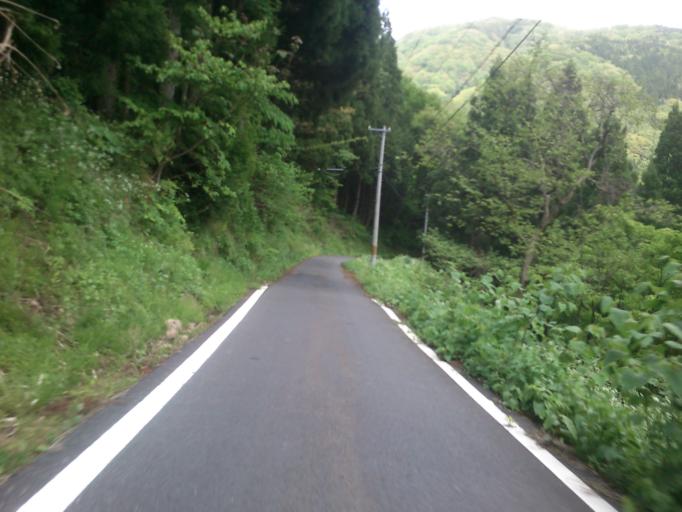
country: JP
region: Kyoto
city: Miyazu
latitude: 35.6546
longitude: 135.1589
